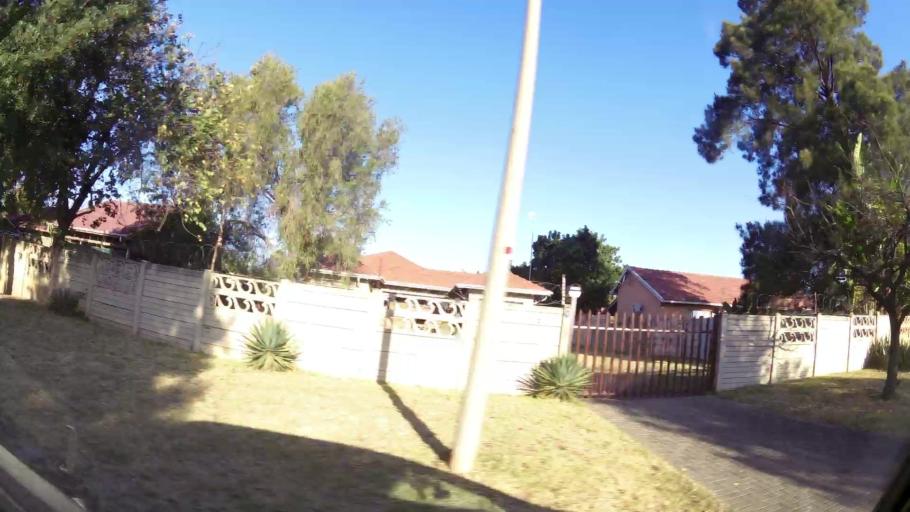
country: ZA
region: North-West
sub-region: Bojanala Platinum District Municipality
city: Rustenburg
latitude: -25.6861
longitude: 27.2139
